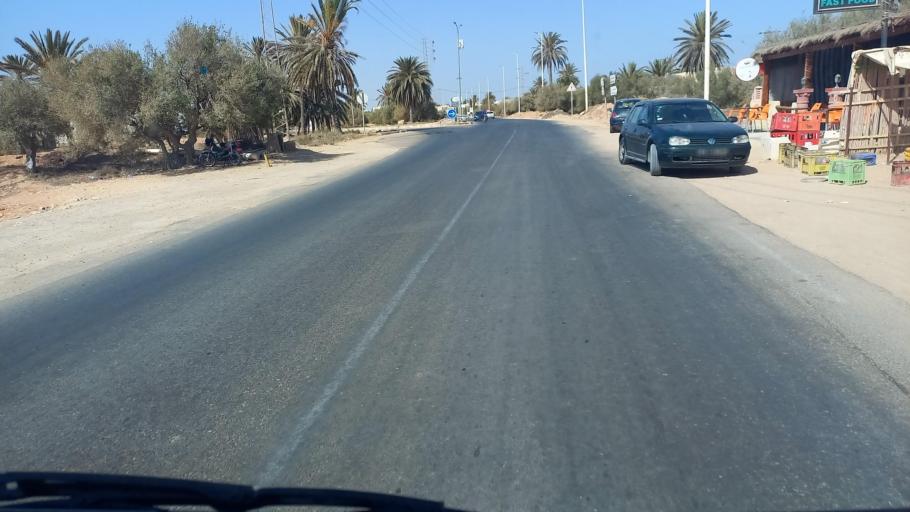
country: TN
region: Madanin
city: Midoun
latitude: 33.7773
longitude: 11.0363
